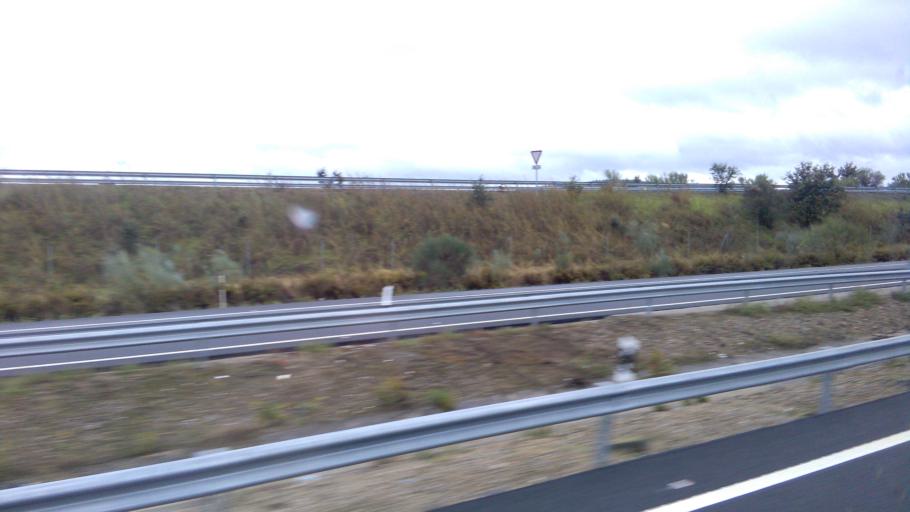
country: ES
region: Extremadura
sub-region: Provincia de Caceres
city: Saucedilla
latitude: 39.8402
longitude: -5.6452
